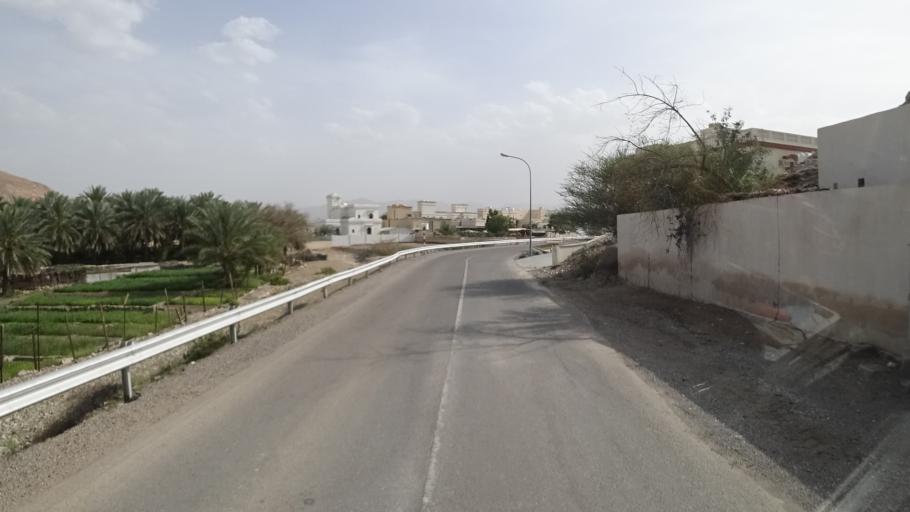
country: OM
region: Muhafazat Masqat
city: Bawshar
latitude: 23.3892
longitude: 58.5175
